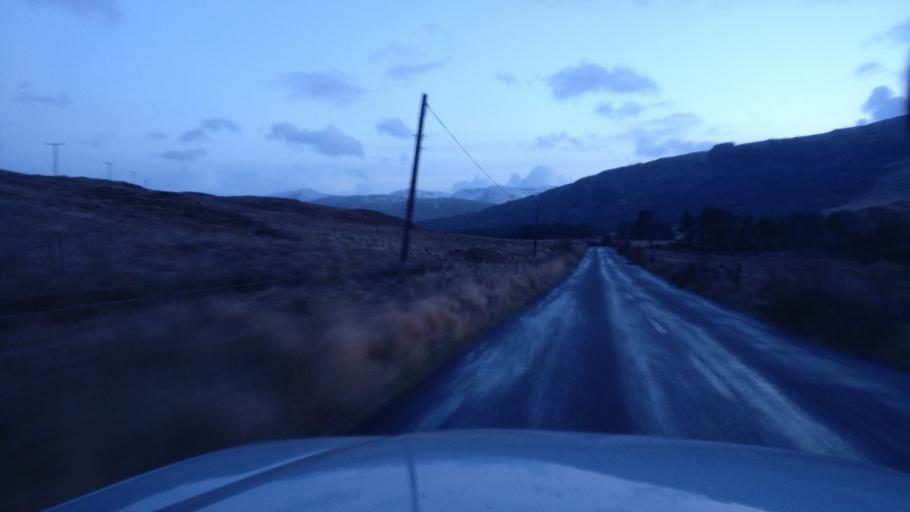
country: IE
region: Connaught
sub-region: Maigh Eo
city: Westport
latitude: 53.5617
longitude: -9.6486
